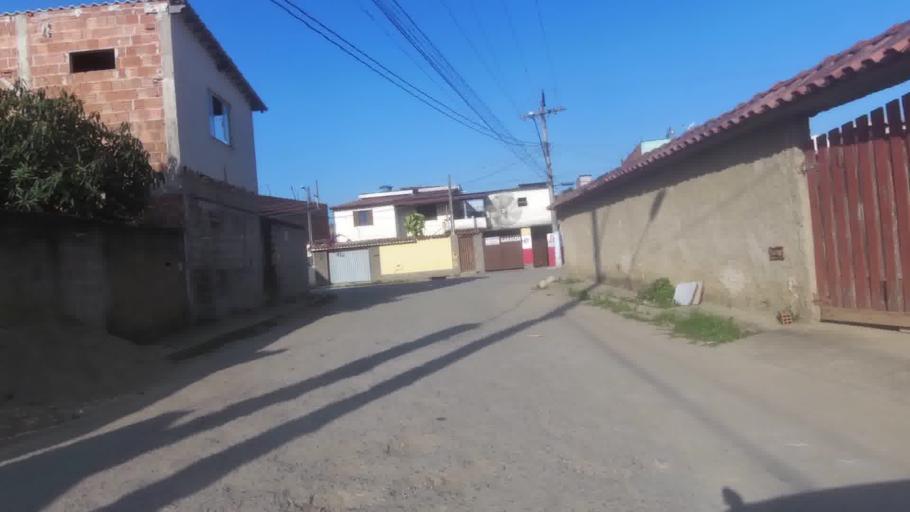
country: BR
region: Espirito Santo
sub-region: Itapemirim
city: Itapemirim
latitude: -21.0188
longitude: -40.8169
